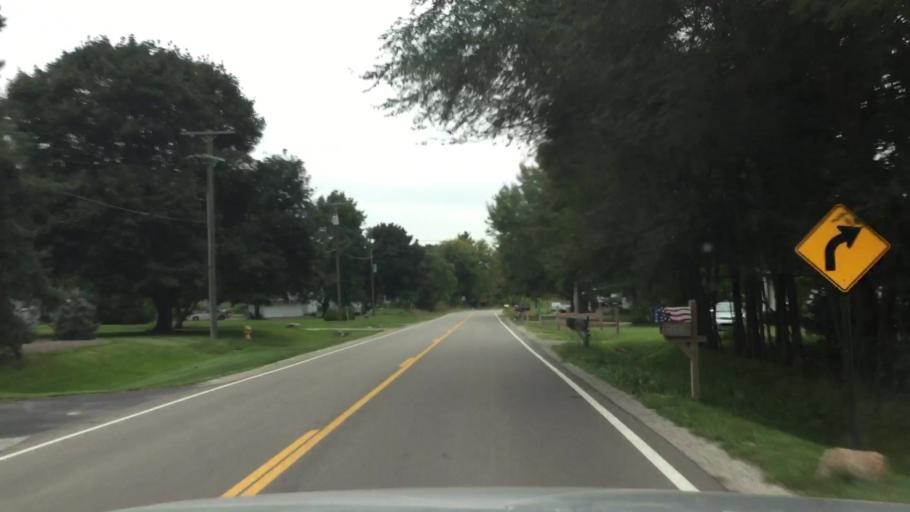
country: US
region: Michigan
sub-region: Washtenaw County
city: Ypsilanti
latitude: 42.1932
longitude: -83.6324
